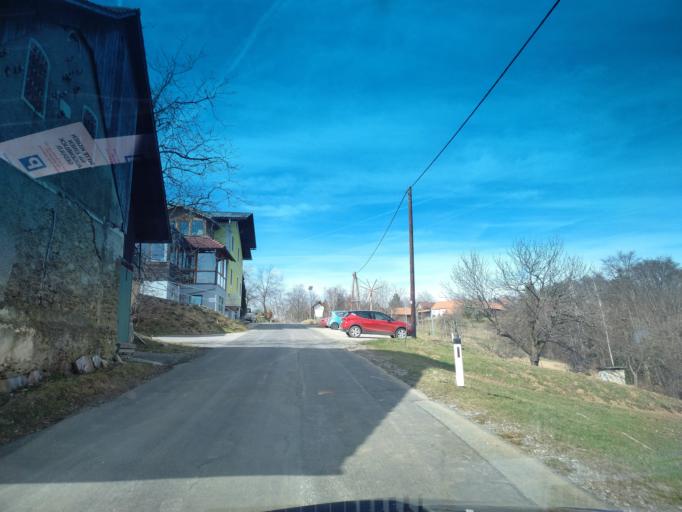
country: AT
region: Styria
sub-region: Politischer Bezirk Leibnitz
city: Kitzeck im Sausal
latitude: 46.7969
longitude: 15.4329
